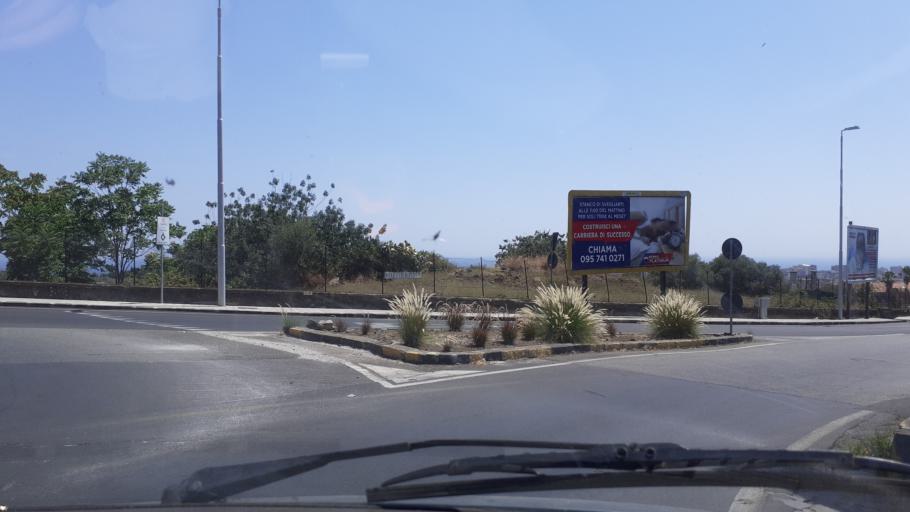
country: IT
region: Sicily
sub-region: Catania
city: Cerza
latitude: 37.5395
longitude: 15.1024
